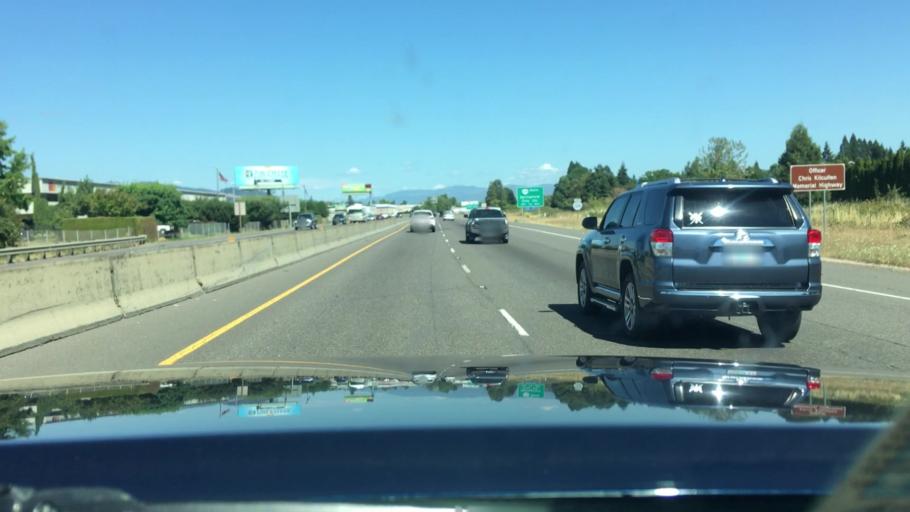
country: US
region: Oregon
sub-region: Lane County
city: Springfield
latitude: 44.0631
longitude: -123.0411
